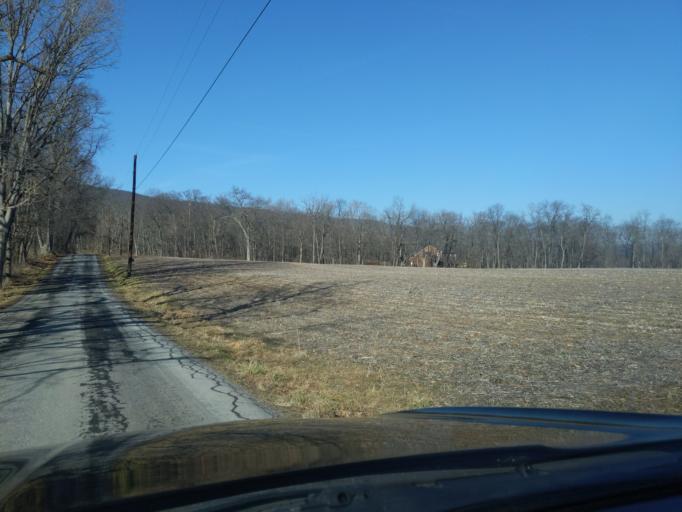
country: US
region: Pennsylvania
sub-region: Blair County
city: Bellwood
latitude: 40.5774
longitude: -78.2720
